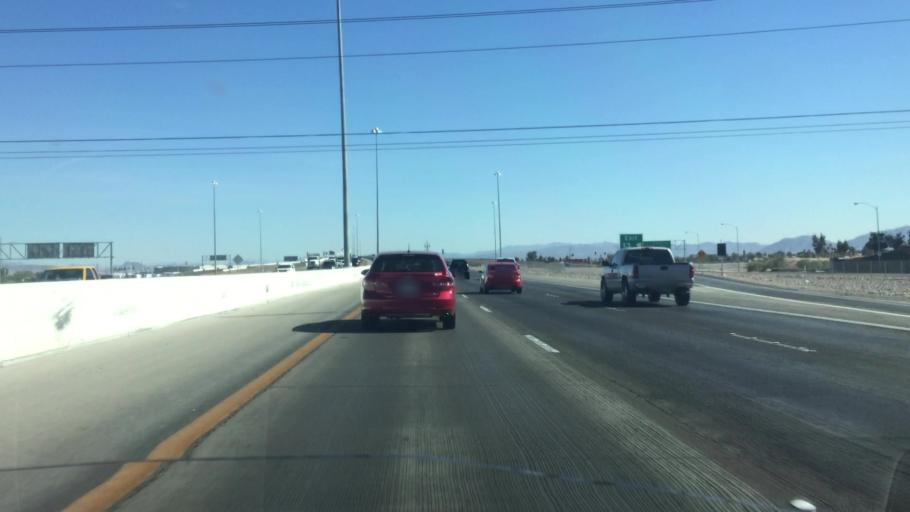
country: US
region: Nevada
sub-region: Clark County
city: Enterprise
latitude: 36.0675
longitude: -115.2127
